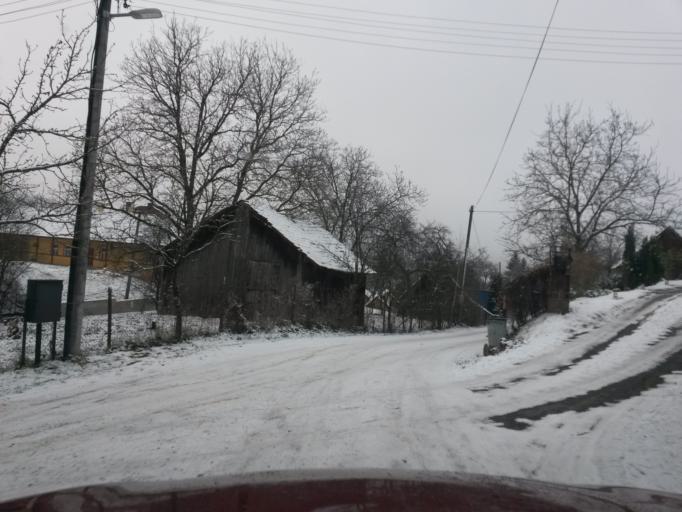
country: SK
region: Presovsky
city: Sabinov
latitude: 48.9866
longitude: 21.0780
